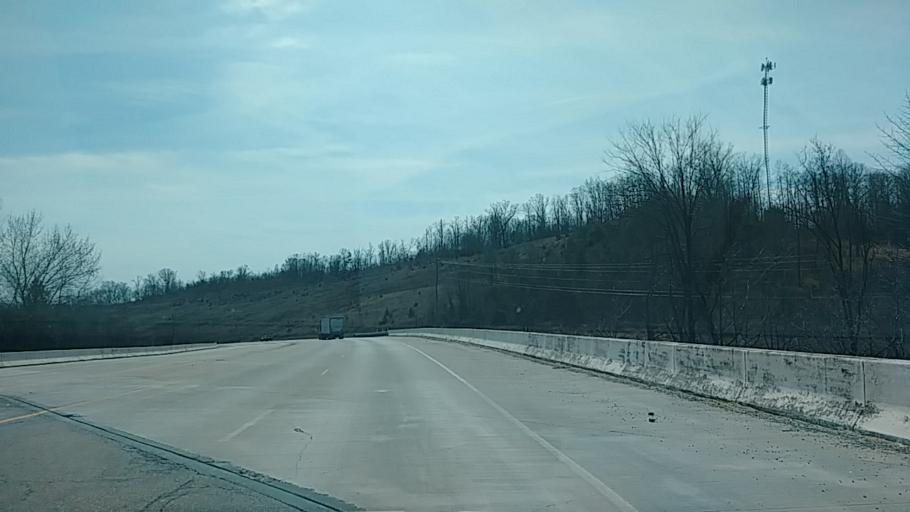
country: US
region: Tennessee
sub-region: Claiborne County
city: Tazewell
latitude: 36.4304
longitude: -83.5573
